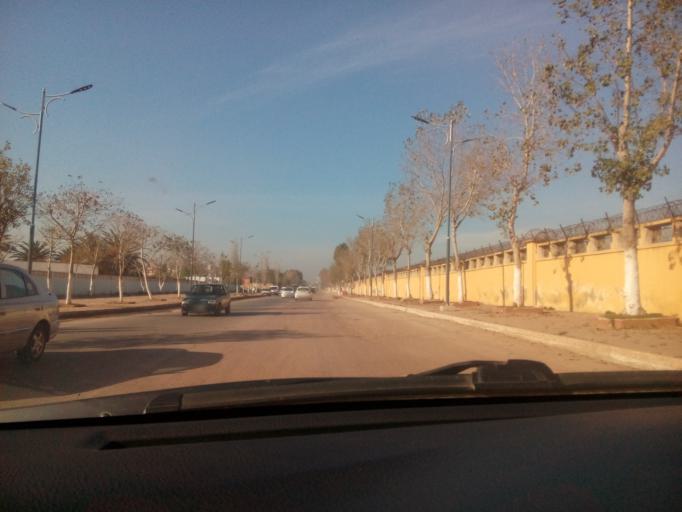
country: DZ
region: Oran
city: Es Senia
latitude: 35.6525
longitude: -0.6137
